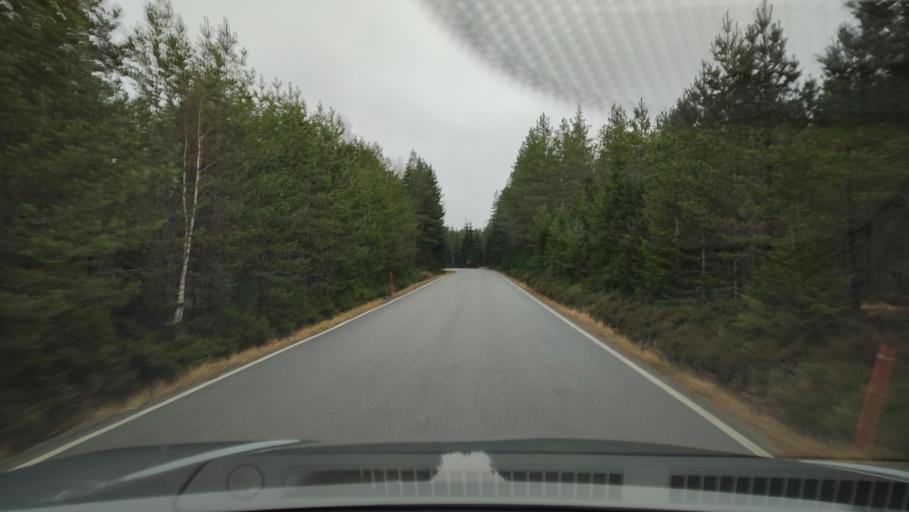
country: FI
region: Southern Ostrobothnia
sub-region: Suupohja
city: Isojoki
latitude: 62.1872
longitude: 21.9424
